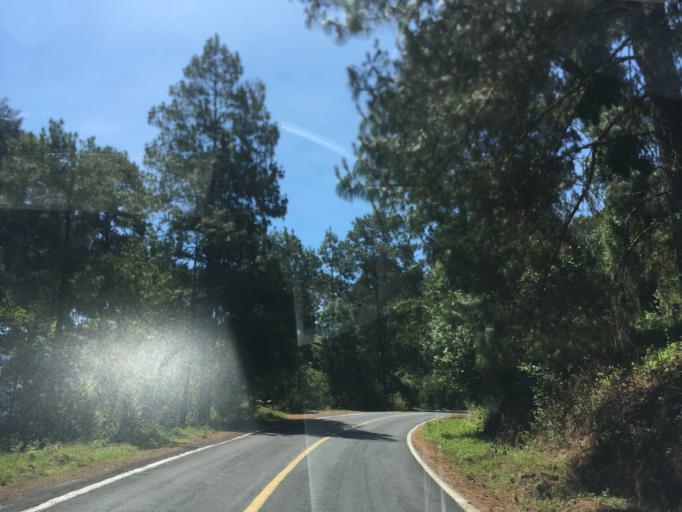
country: MX
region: Michoacan
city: Tzitzio
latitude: 19.6361
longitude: -100.7836
